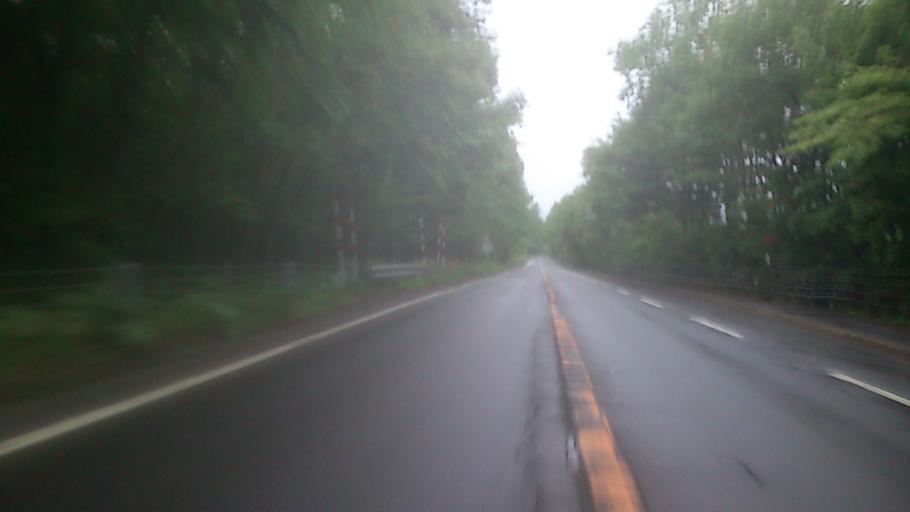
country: JP
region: Hokkaido
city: Tomakomai
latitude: 42.7608
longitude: 141.4248
